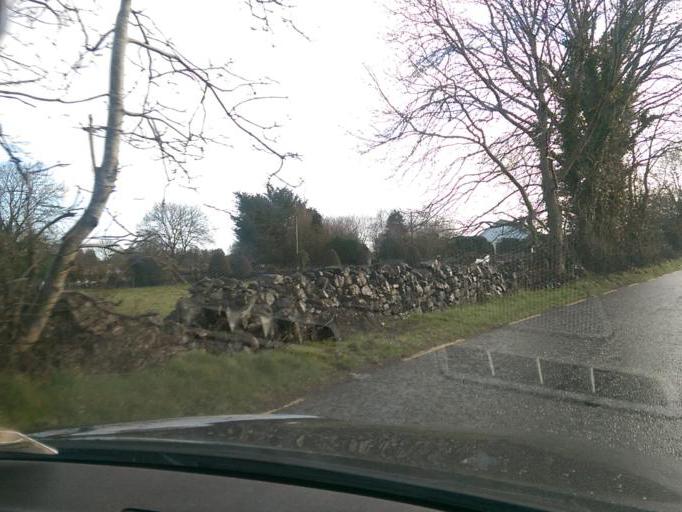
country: IE
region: Connaught
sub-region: County Galway
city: Athenry
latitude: 53.3378
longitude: -8.8072
